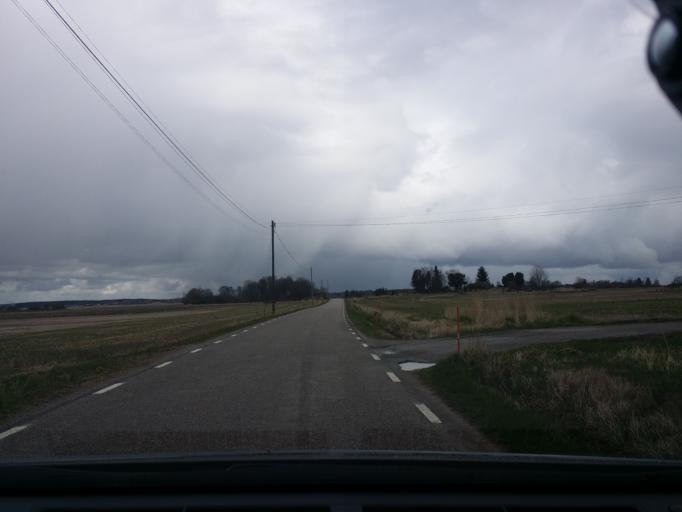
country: SE
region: Uppsala
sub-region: Enkopings Kommun
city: Enkoping
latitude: 59.6714
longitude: 17.0251
